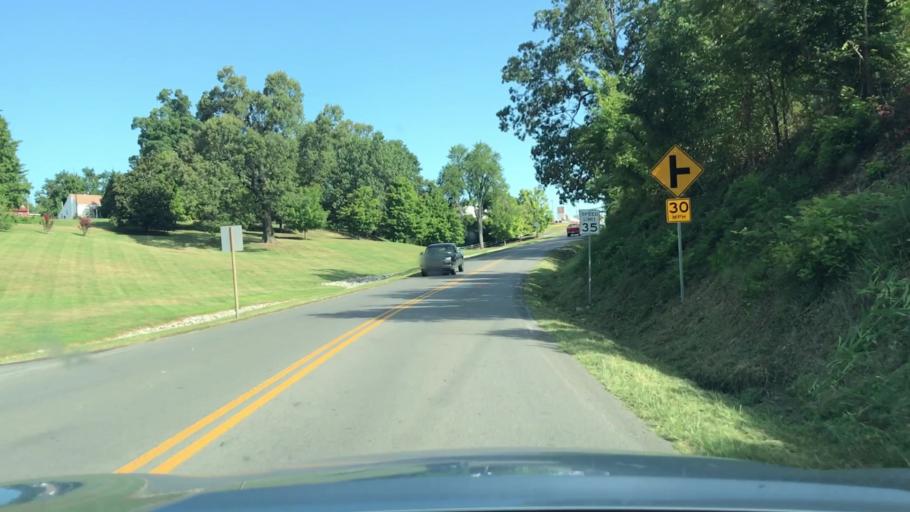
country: US
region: Kentucky
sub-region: Muhlenberg County
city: Greenville
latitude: 37.1964
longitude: -87.1768
